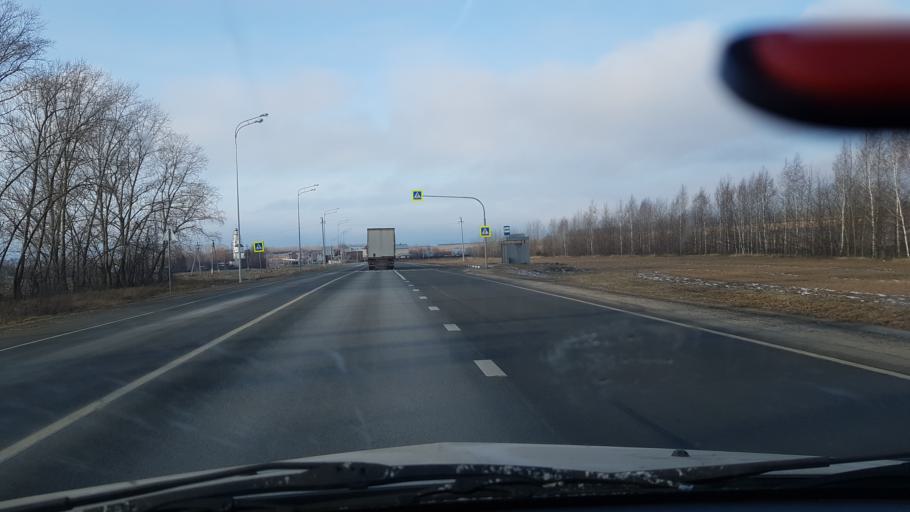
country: RU
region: Tatarstan
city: Laishevo
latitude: 55.3913
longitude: 49.8093
